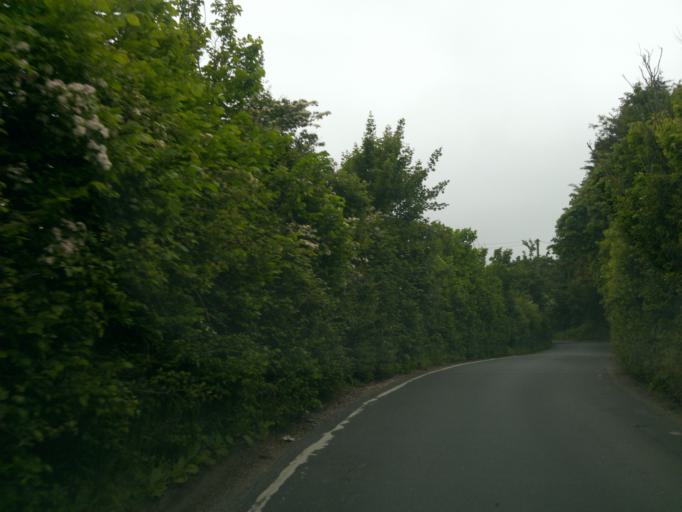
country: GB
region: England
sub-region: Essex
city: West Bergholt
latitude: 51.8972
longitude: 0.8653
